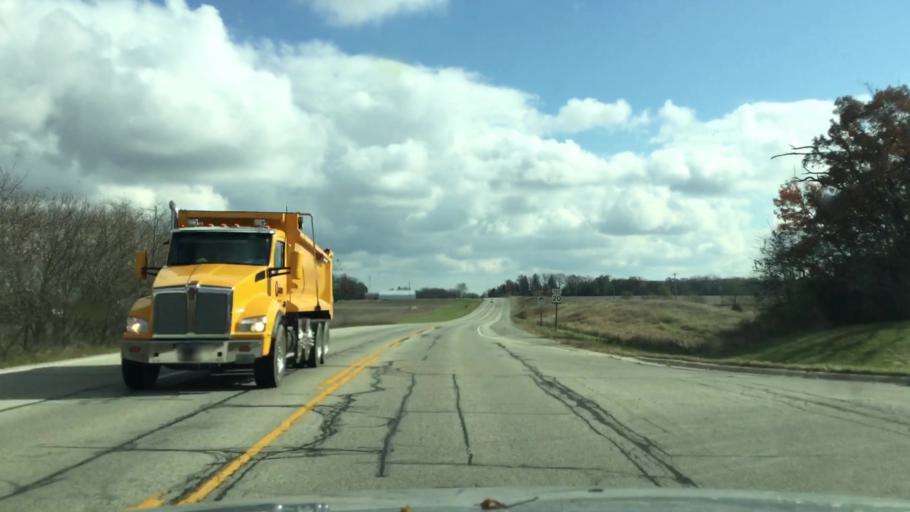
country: US
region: Wisconsin
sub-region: Racine County
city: Eagle Lake
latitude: 42.7427
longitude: -88.1454
